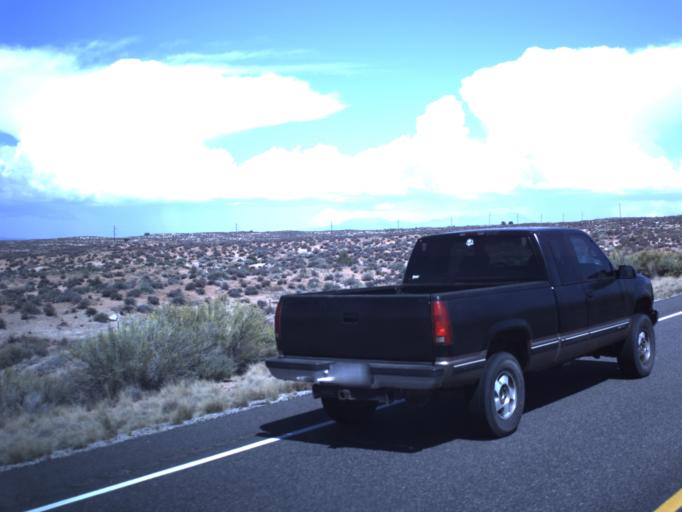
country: US
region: Utah
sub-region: San Juan County
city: Blanding
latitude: 37.3643
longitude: -109.5105
